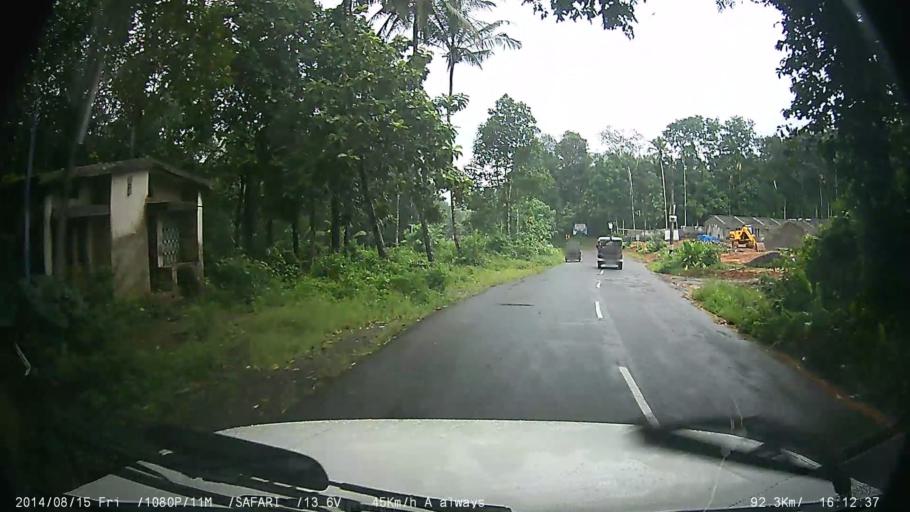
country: IN
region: Kerala
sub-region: Kottayam
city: Lalam
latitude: 9.7413
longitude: 76.6960
